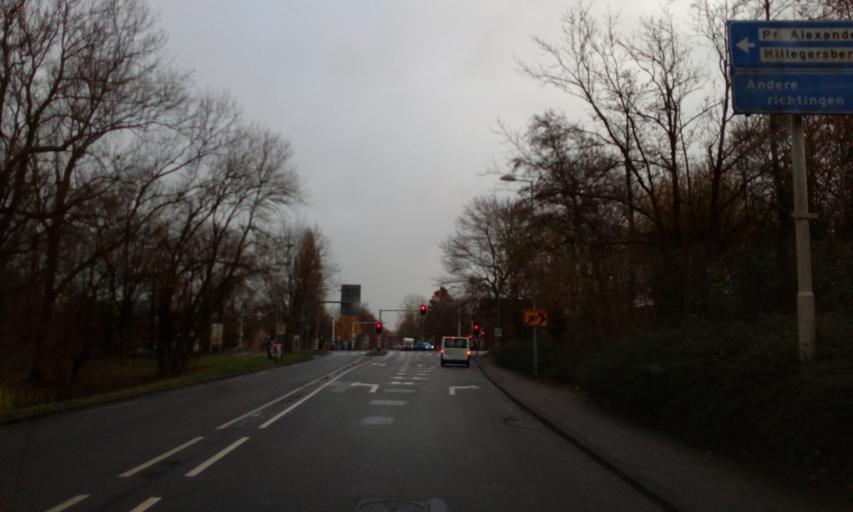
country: NL
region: South Holland
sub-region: Gemeente Rotterdam
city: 's-Gravenland
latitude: 51.9272
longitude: 4.5328
